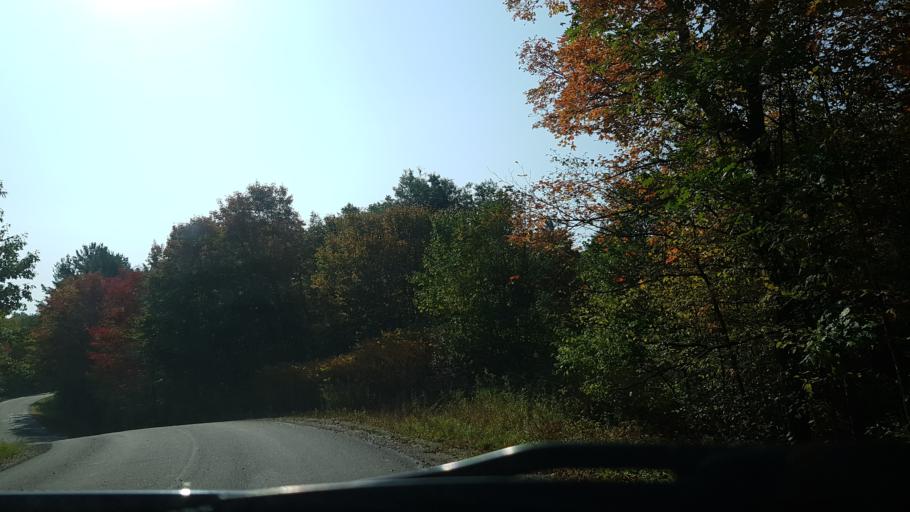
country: CA
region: Ontario
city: Bracebridge
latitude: 44.9718
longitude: -79.2585
